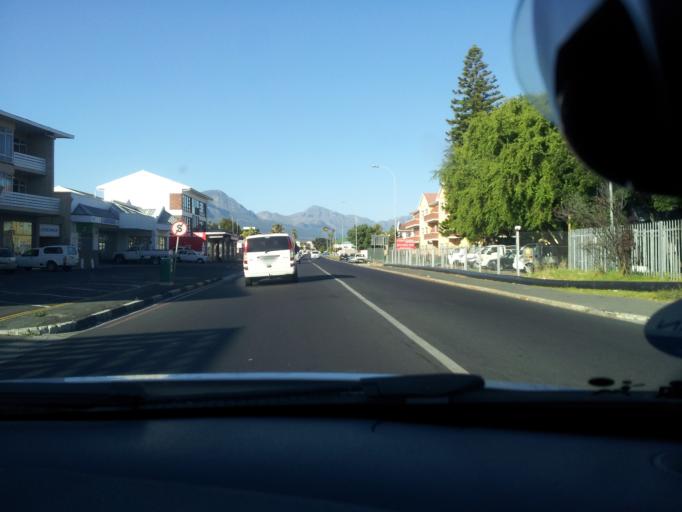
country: ZA
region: Western Cape
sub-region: Cape Winelands District Municipality
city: Stellenbosch
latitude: -34.1142
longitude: 18.8321
